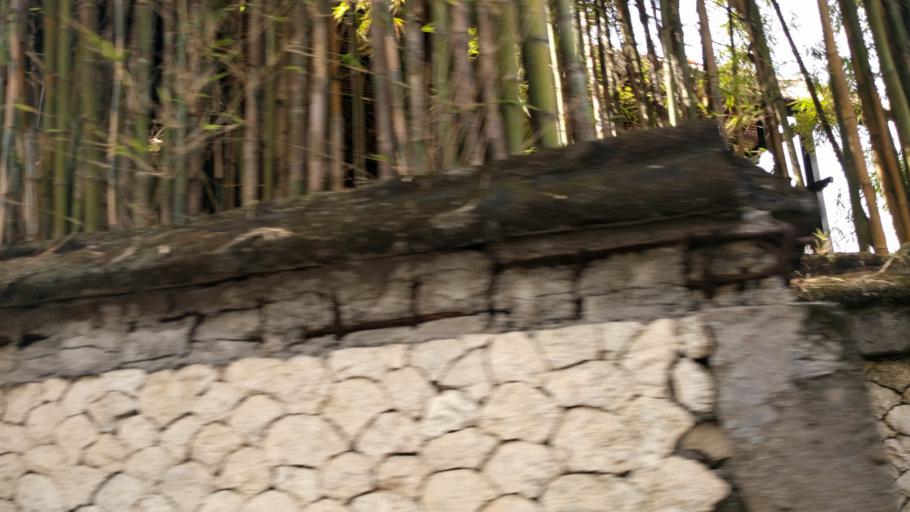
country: ID
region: Bali
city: Kuta
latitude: -8.6909
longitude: 115.1580
